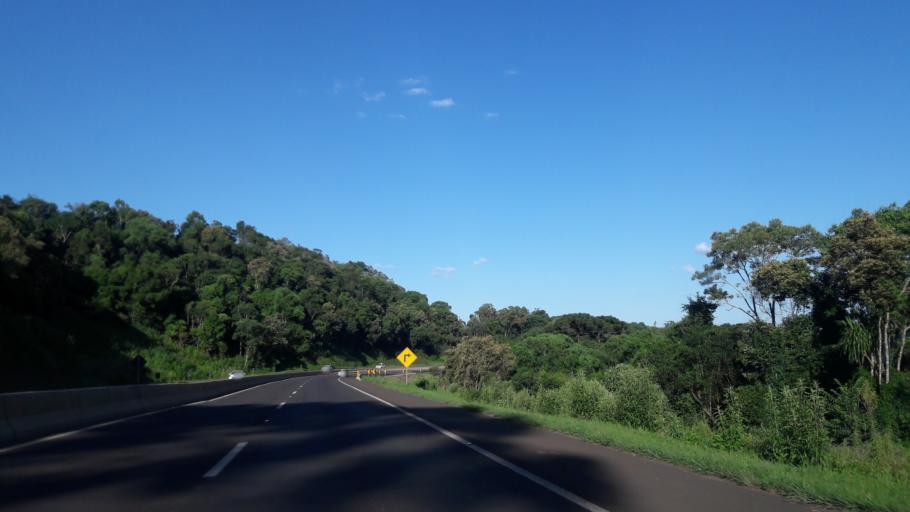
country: BR
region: Parana
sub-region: Guarapuava
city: Guarapuava
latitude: -25.3468
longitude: -51.3870
